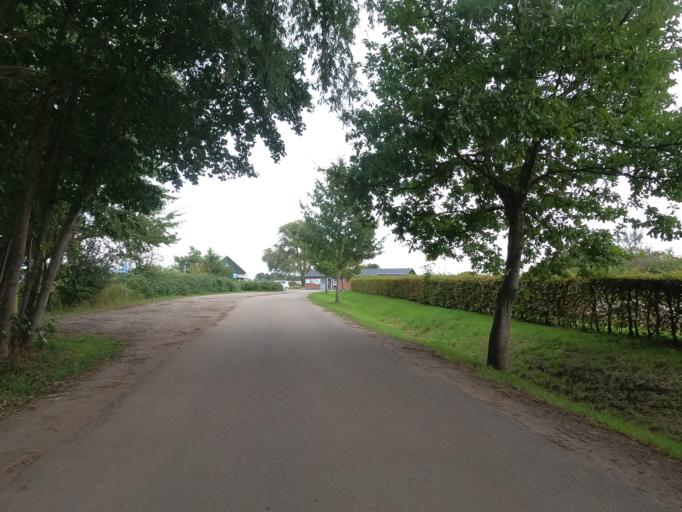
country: DE
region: Schleswig-Holstein
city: Grossenbrode
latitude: 54.3439
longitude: 11.0616
